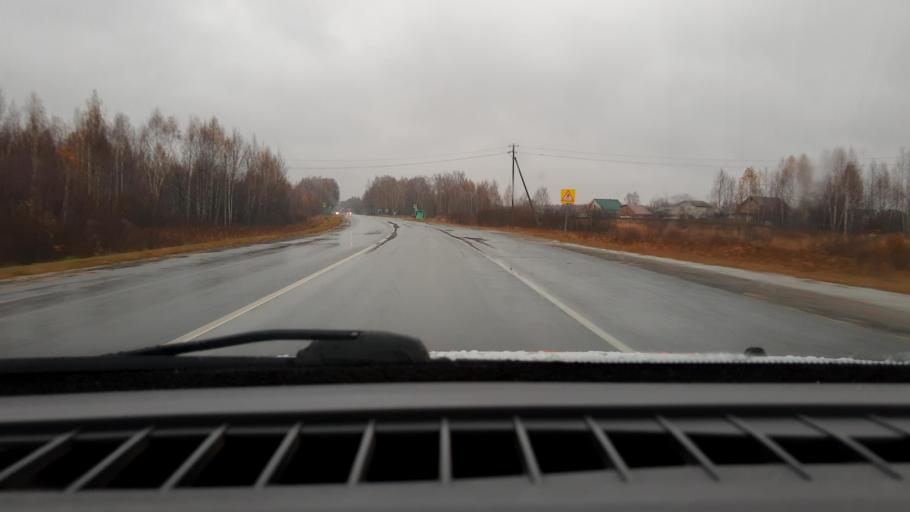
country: RU
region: Nizjnij Novgorod
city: Sitniki
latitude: 56.5252
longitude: 44.0264
